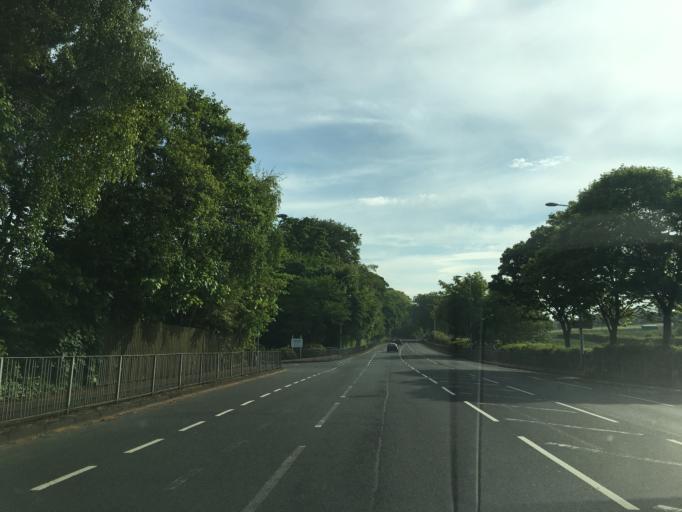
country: GB
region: Scotland
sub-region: Midlothian
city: Penicuik
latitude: 55.8412
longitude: -3.2122
